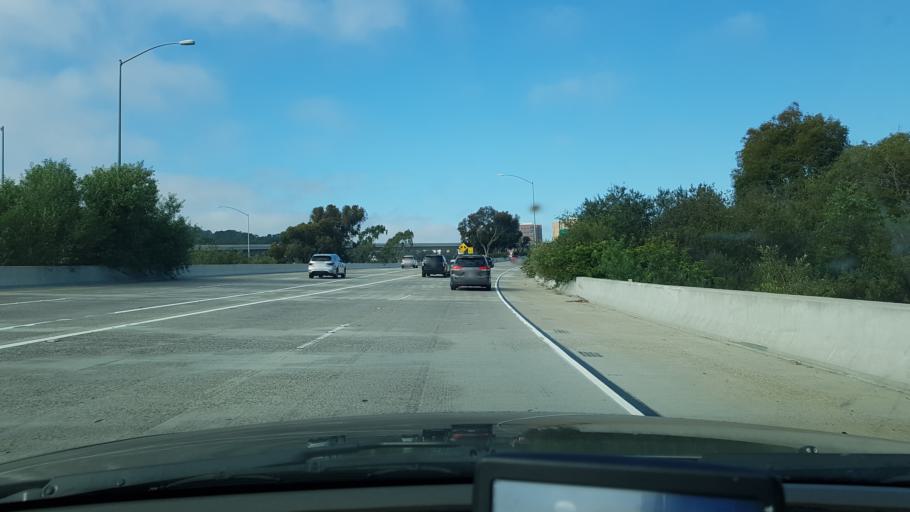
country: US
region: California
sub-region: San Diego County
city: Del Mar
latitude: 32.9292
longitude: -117.2401
